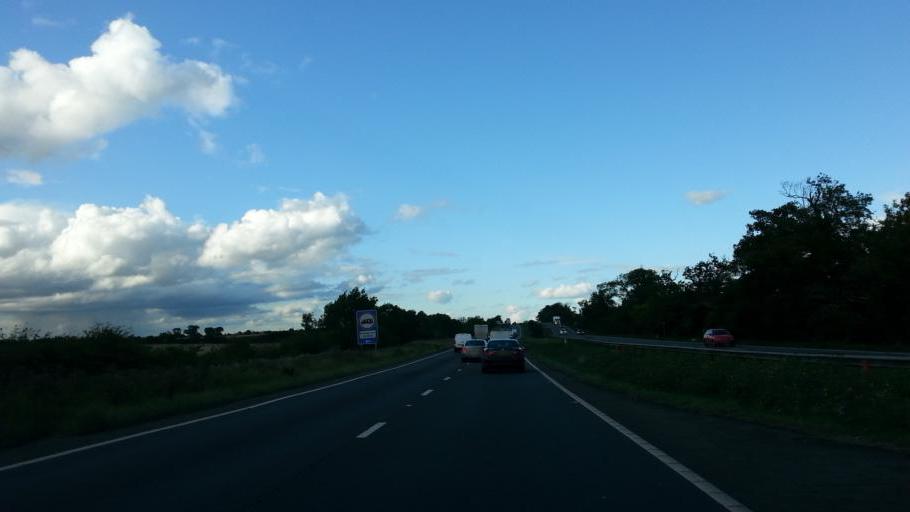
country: GB
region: England
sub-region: District of Rutland
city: Greetham
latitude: 52.7741
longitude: -0.6114
